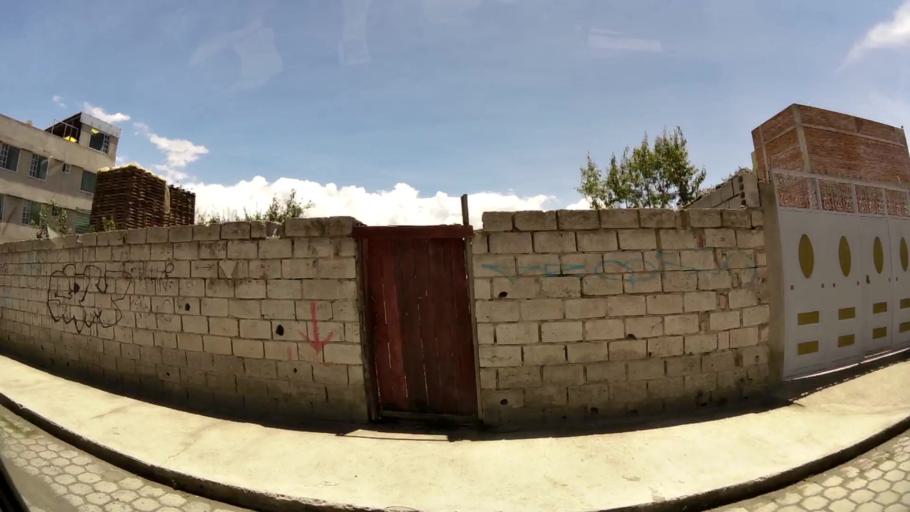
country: EC
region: Chimborazo
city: Riobamba
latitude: -1.6822
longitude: -78.6518
